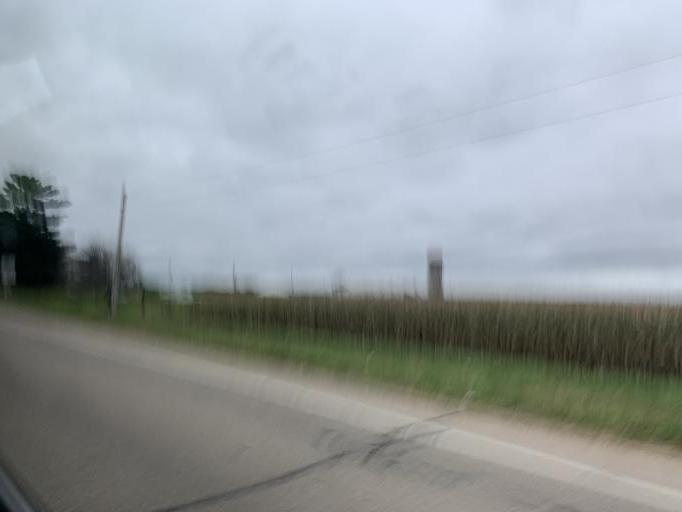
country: US
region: Wisconsin
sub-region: Grant County
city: Muscoda
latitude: 43.2197
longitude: -90.4755
